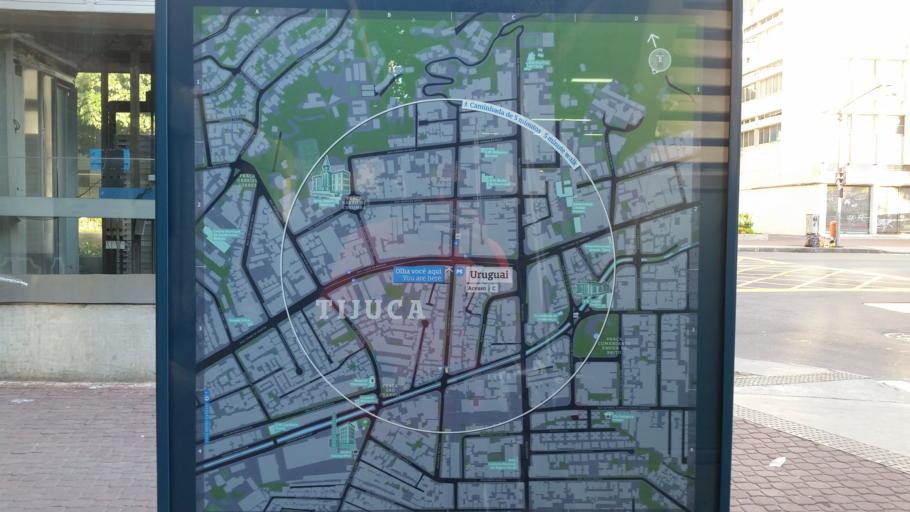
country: BR
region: Rio de Janeiro
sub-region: Rio De Janeiro
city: Rio de Janeiro
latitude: -22.9316
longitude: -43.2396
